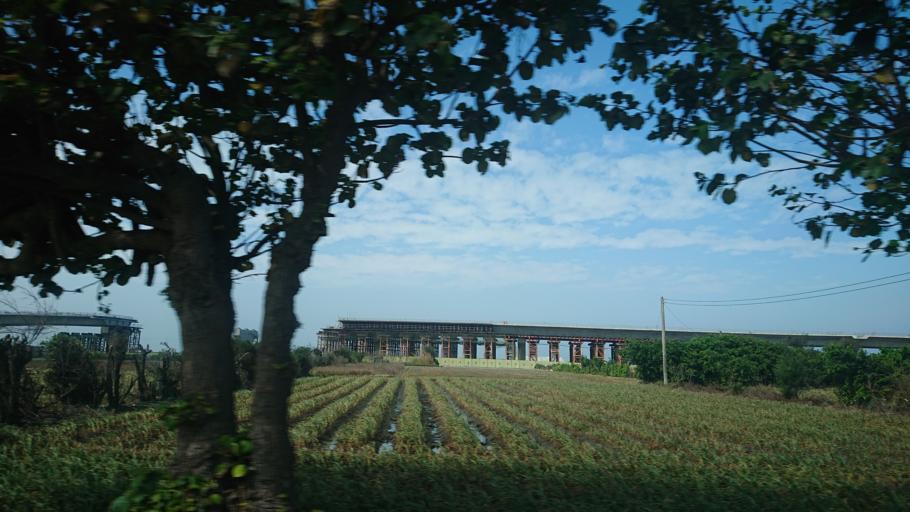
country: TW
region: Taiwan
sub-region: Changhua
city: Chang-hua
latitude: 23.9141
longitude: 120.3114
